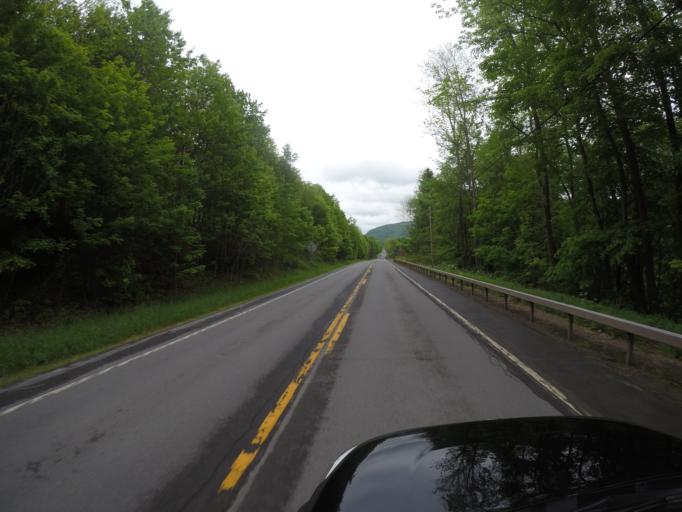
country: US
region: New York
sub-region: Delaware County
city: Delhi
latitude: 42.2555
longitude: -74.9180
